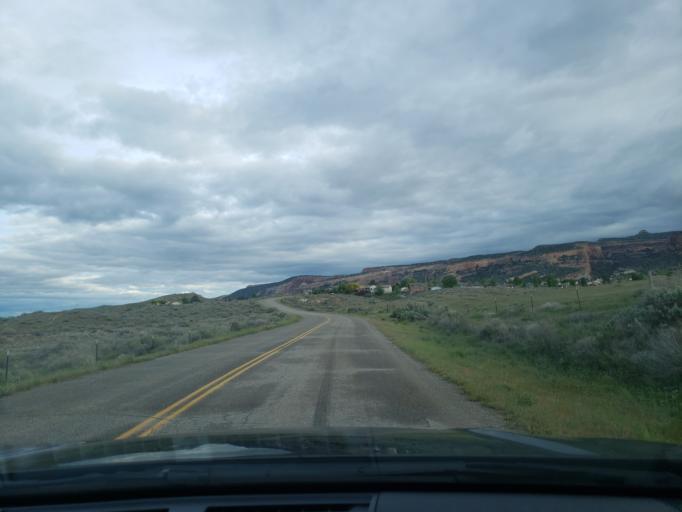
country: US
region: Colorado
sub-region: Mesa County
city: Fruita
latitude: 39.1424
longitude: -108.7444
